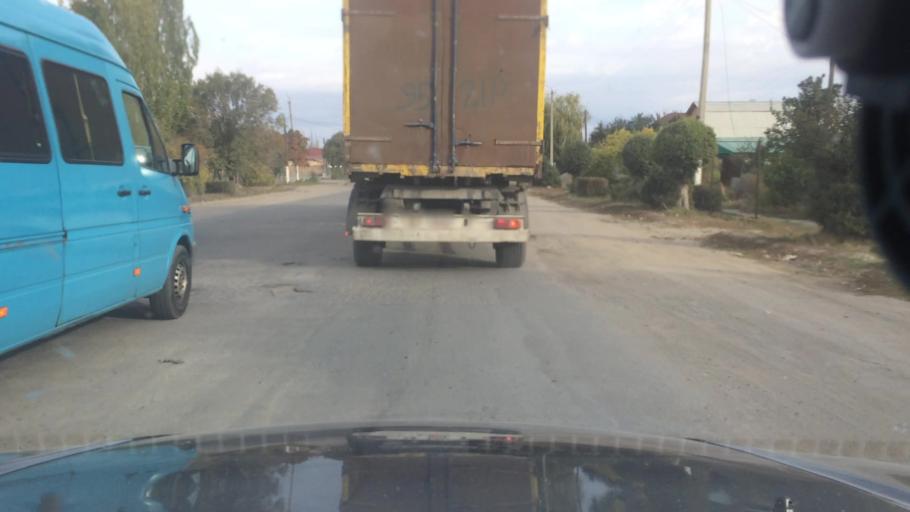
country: KG
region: Ysyk-Koel
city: Karakol
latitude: 42.5168
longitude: 78.3858
